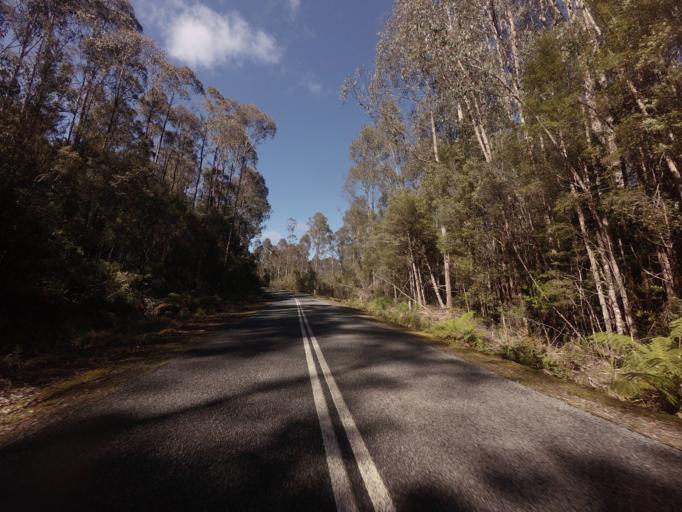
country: AU
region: Tasmania
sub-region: Huon Valley
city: Geeveston
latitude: -42.7793
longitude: 146.3984
